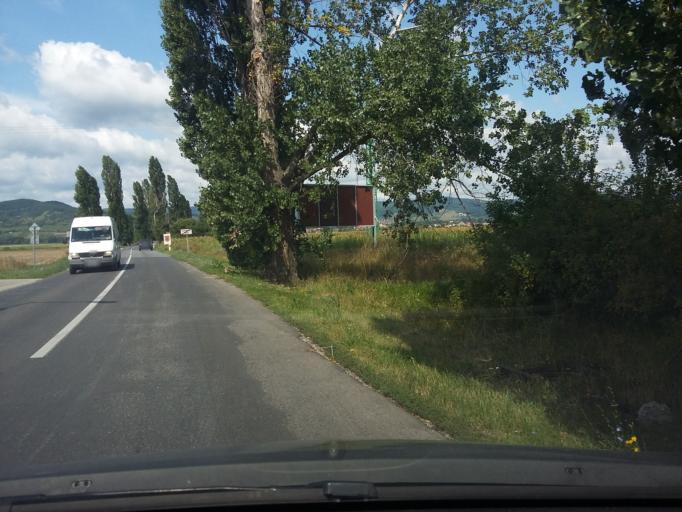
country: SK
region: Bratislavsky
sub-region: Okres Pezinok
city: Pezinok
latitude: 48.2567
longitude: 17.2635
